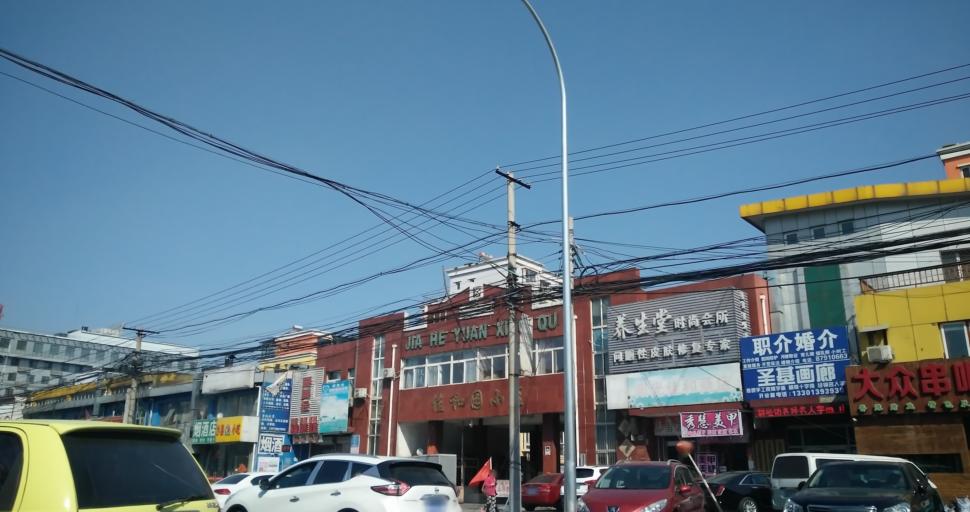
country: CN
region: Beijing
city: Jiugong
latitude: 39.8045
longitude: 116.4378
